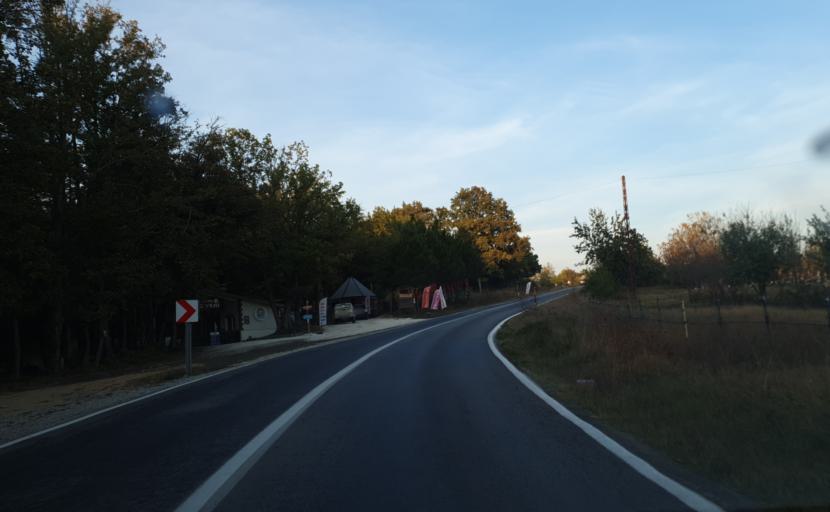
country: TR
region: Kirklareli
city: Sergen
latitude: 41.8402
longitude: 27.7999
